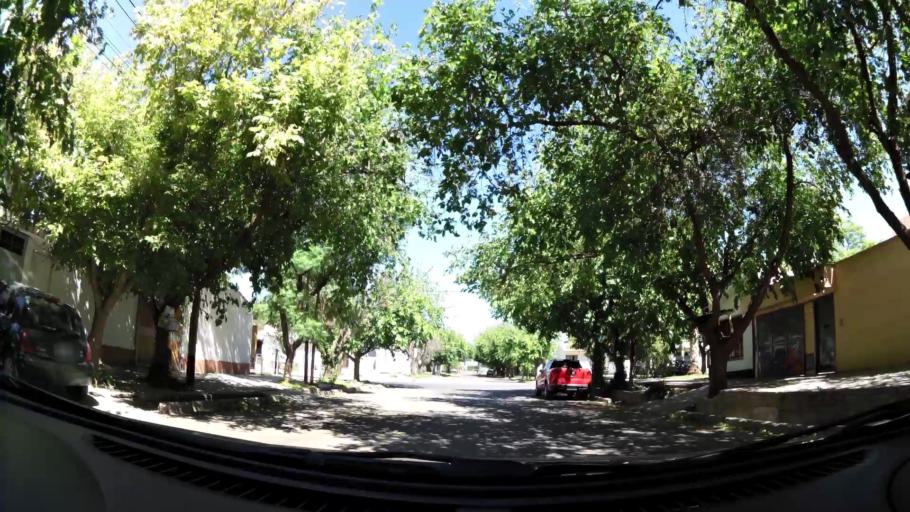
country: AR
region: Mendoza
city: Las Heras
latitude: -32.8499
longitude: -68.8505
